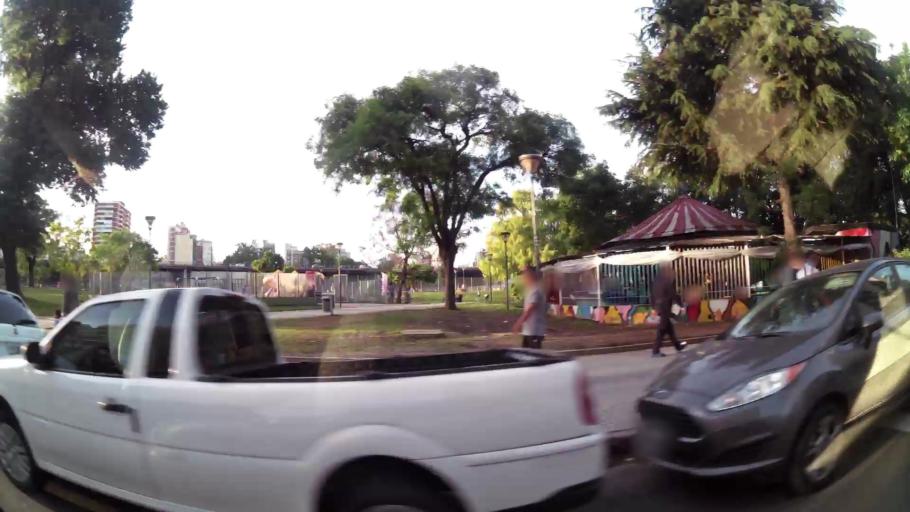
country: AR
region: Buenos Aires F.D.
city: Villa Santa Rita
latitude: -34.6363
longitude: -58.4441
